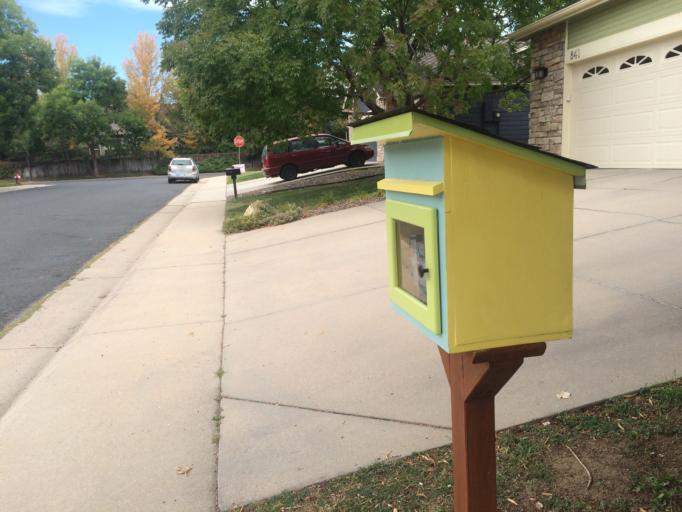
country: US
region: Colorado
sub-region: Boulder County
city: Superior
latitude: 39.9676
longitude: -105.1583
